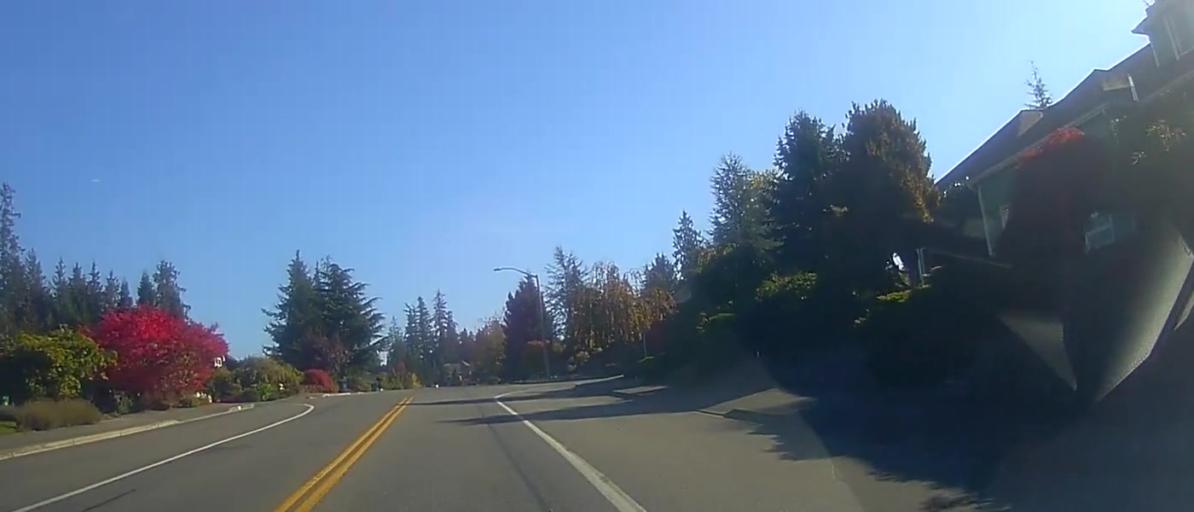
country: US
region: Washington
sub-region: Skagit County
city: Mount Vernon
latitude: 48.4264
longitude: -122.2905
